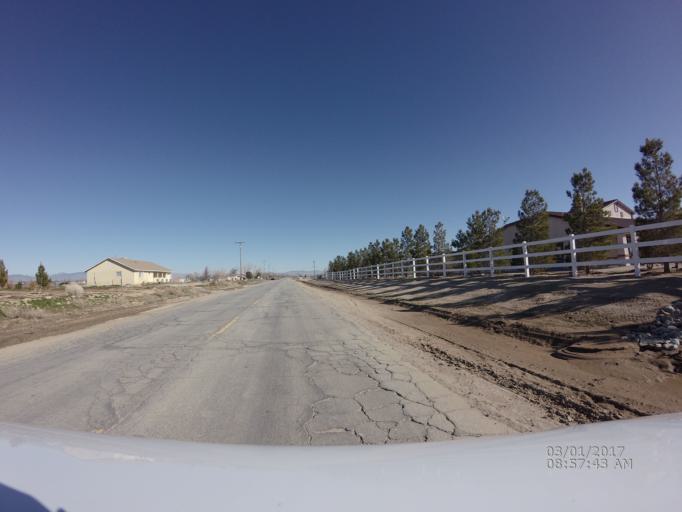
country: US
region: California
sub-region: Los Angeles County
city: Quartz Hill
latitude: 34.7513
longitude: -118.2723
